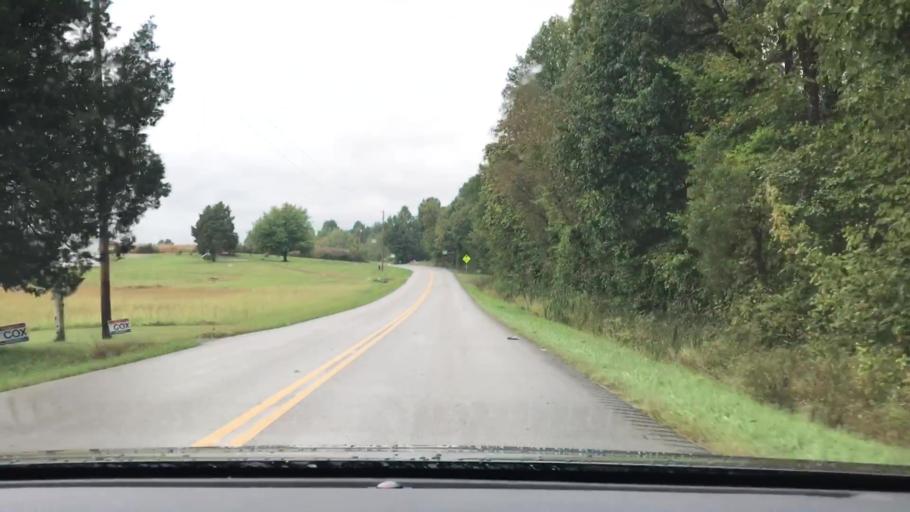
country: US
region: Kentucky
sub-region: McLean County
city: Calhoun
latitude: 37.4889
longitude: -87.2460
